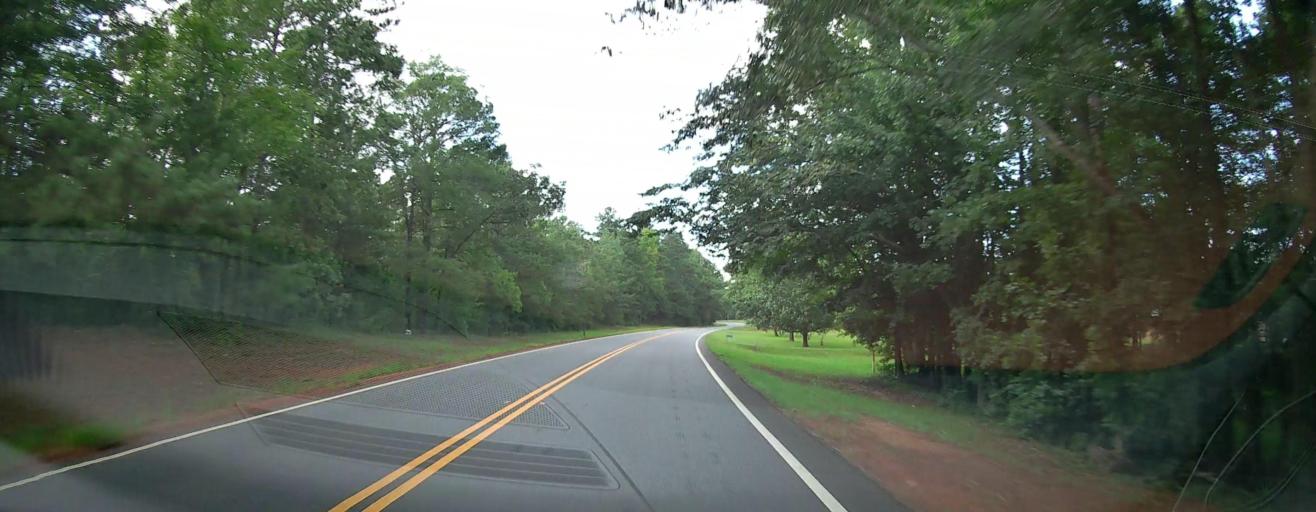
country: US
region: Georgia
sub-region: Bibb County
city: West Point
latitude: 32.8778
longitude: -83.9269
